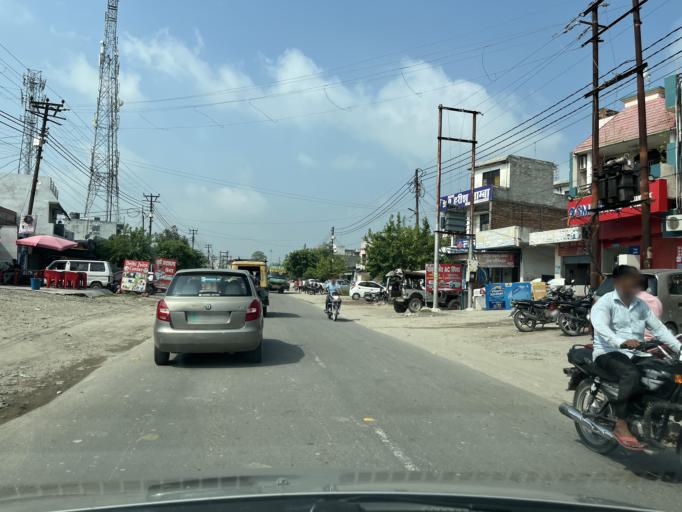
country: IN
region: Uttarakhand
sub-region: Udham Singh Nagar
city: Bazpur
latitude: 29.1547
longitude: 79.1458
